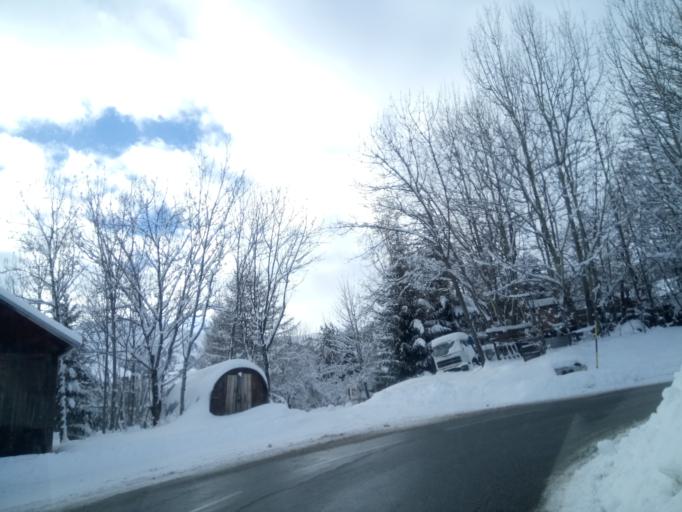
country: FR
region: Rhone-Alpes
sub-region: Departement de la Savoie
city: Saint-Jean-de-Maurienne
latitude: 45.2517
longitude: 6.2909
